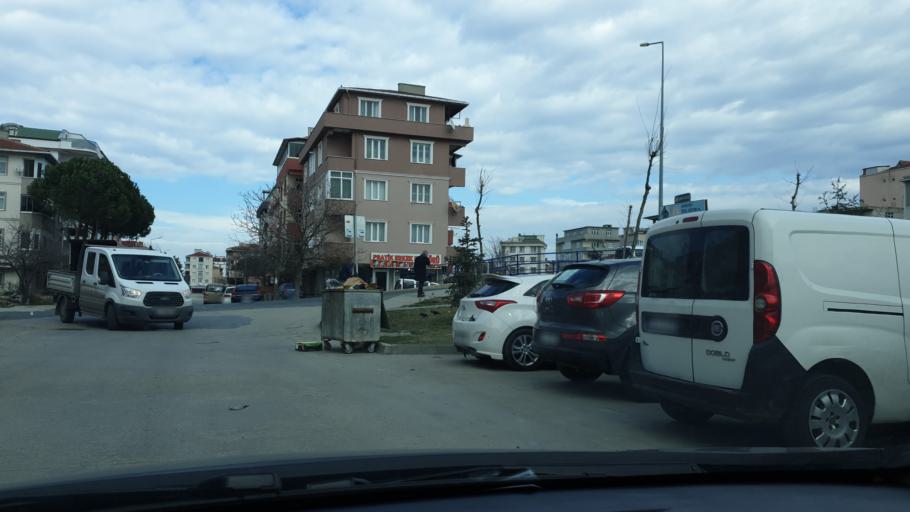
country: TR
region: Tekirdag
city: Cerkezkoey
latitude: 41.2856
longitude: 28.0045
